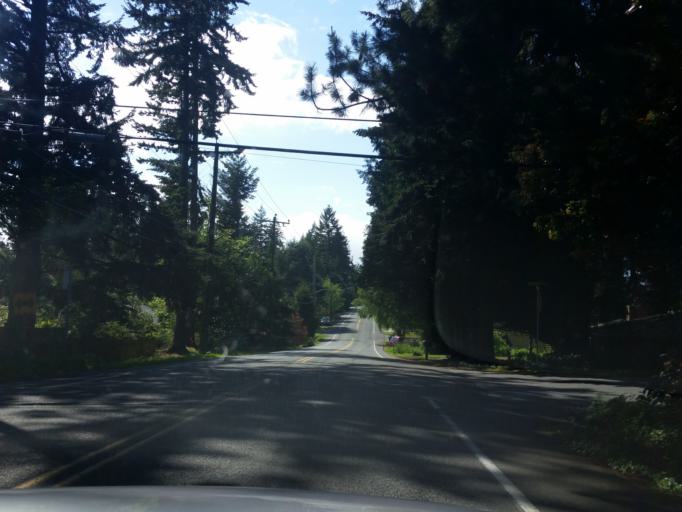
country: US
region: Washington
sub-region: Snohomish County
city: Esperance
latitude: 47.7741
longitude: -122.3556
